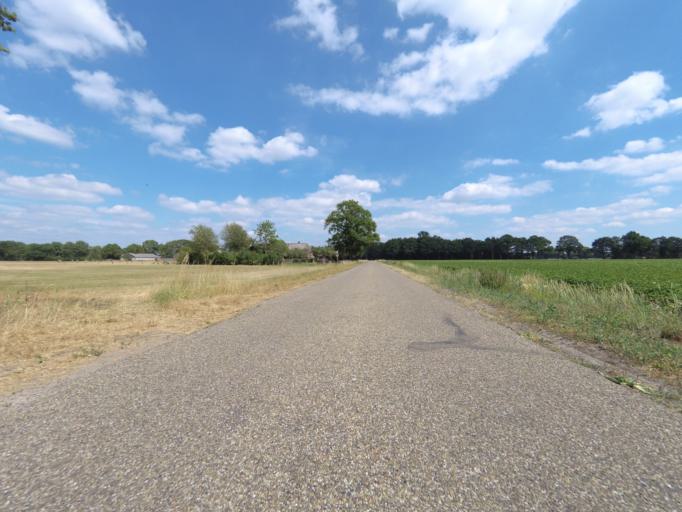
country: NL
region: Overijssel
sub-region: Gemeente Wierden
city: Wierden
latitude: 52.3464
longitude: 6.5334
